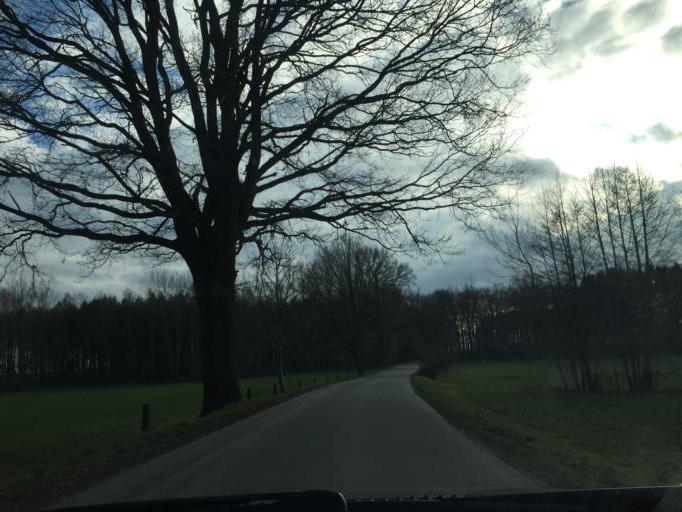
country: DE
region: Saxony
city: Ebersbach
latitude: 51.2114
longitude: 13.6723
